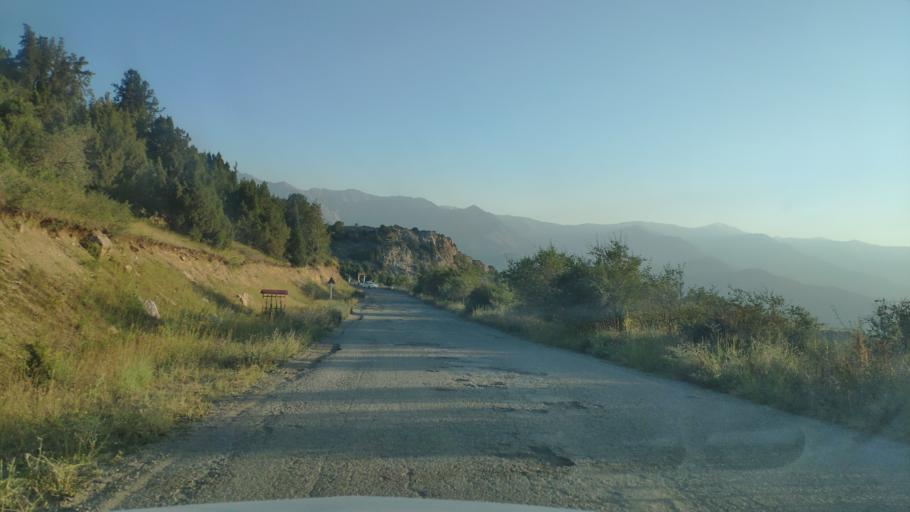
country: TJ
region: Viloyati Sughd
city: Ayni
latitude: 39.6368
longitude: 68.4631
